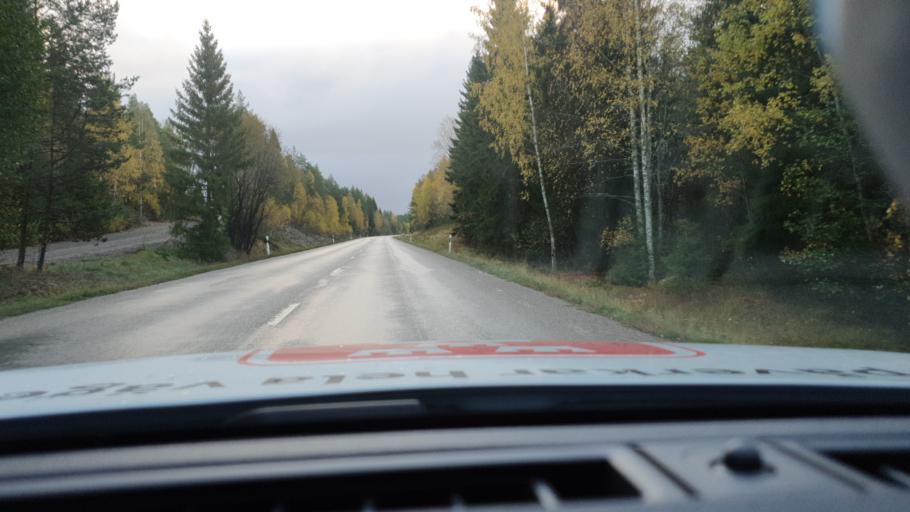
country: SE
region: Uppsala
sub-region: Tierps Kommun
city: Orbyhus
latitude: 60.2105
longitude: 17.7726
